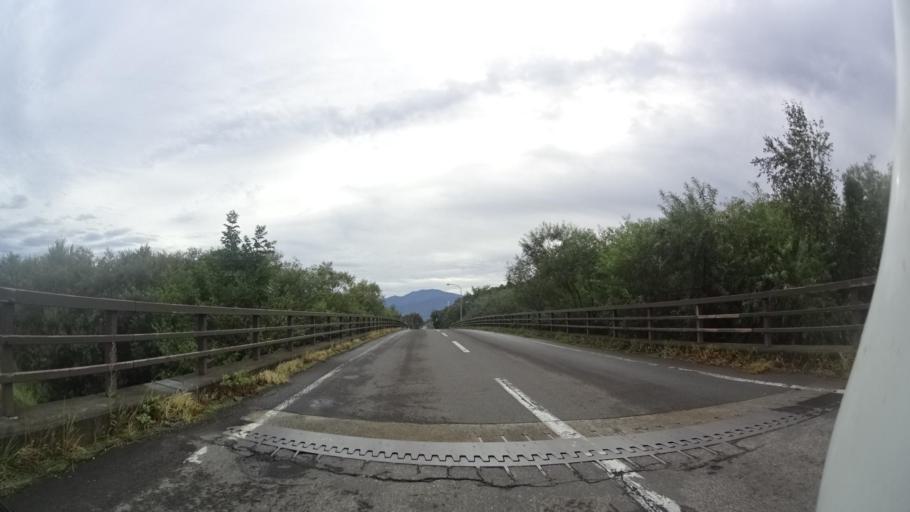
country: JP
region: Hokkaido
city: Abashiri
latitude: 43.8709
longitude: 144.6701
